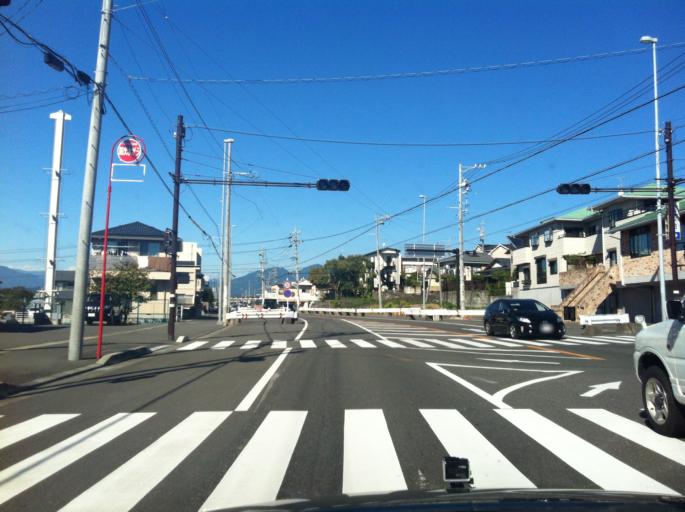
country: JP
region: Shizuoka
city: Shizuoka-shi
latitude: 34.9553
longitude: 138.4287
